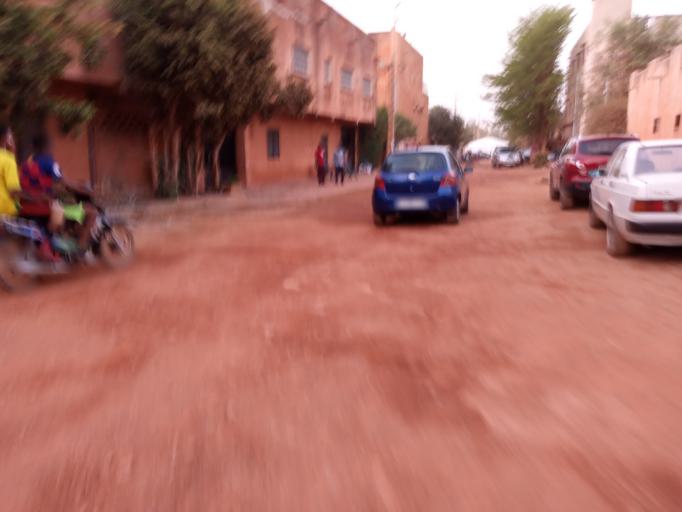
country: ML
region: Bamako
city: Bamako
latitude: 12.5819
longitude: -7.9526
